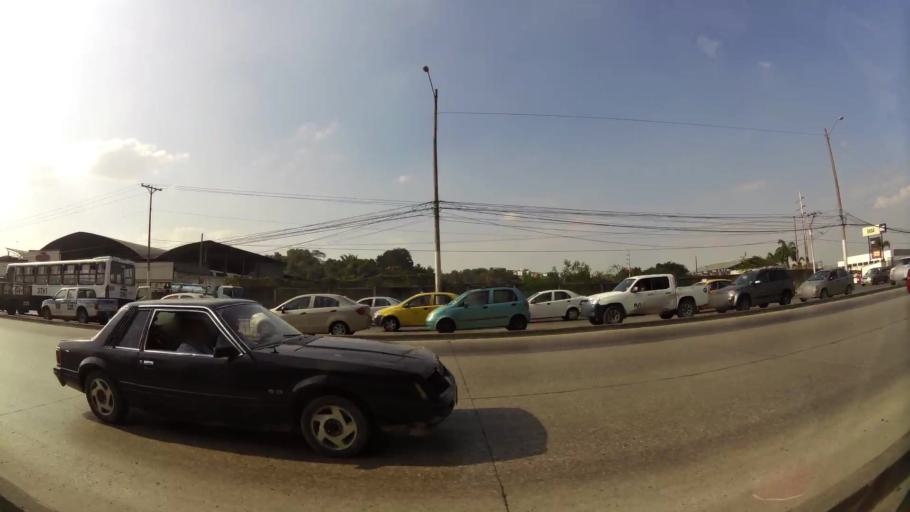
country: EC
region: Guayas
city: Guayaquil
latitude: -2.1422
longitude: -79.9227
